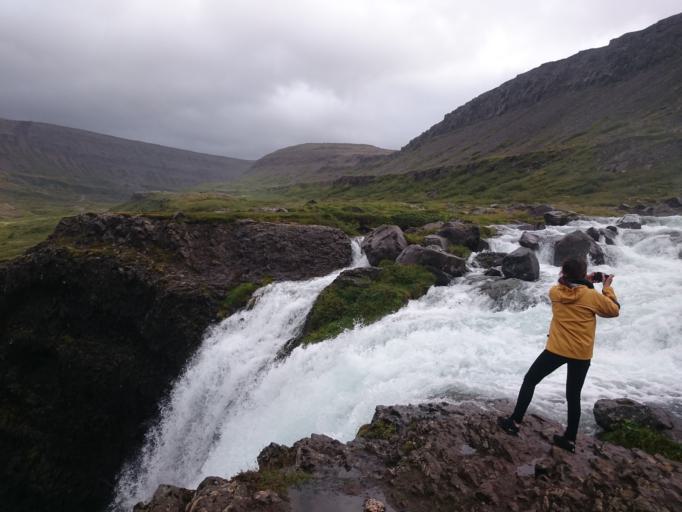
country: IS
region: Westfjords
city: Isafjoerdur
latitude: 65.7337
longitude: -23.2033
